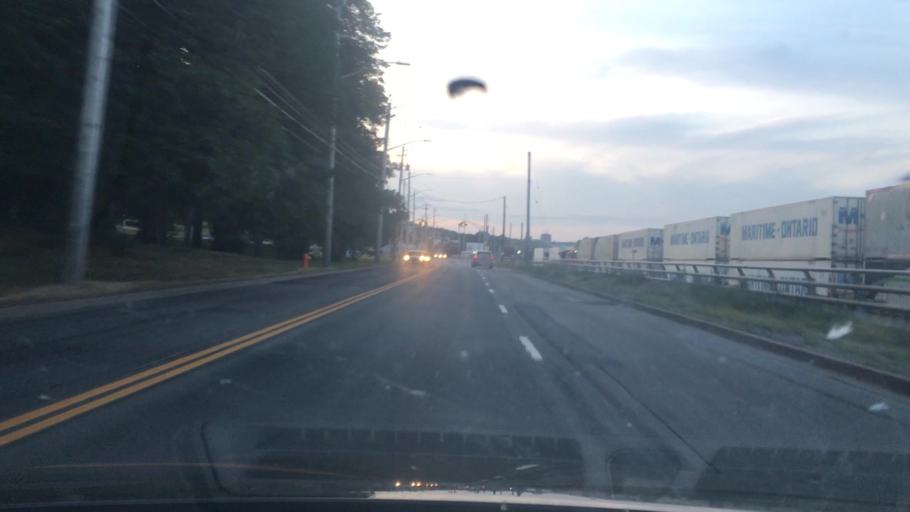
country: CA
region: Nova Scotia
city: Dartmouth
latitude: 44.6716
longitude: -63.6428
